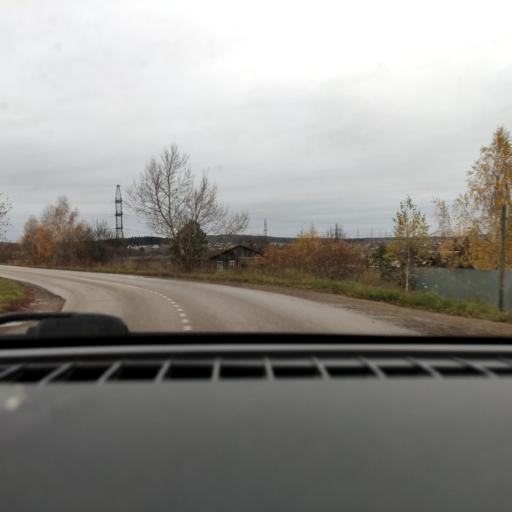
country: RU
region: Perm
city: Ferma
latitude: 57.9268
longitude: 56.3324
